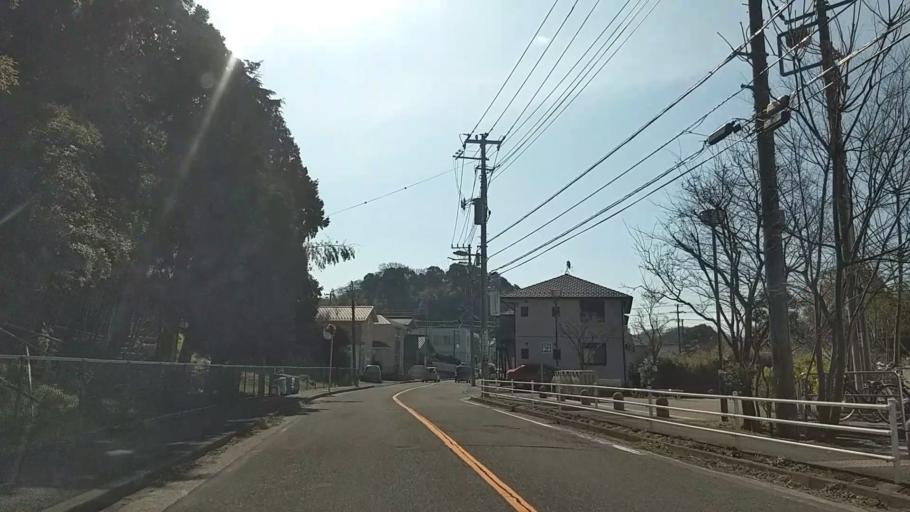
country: JP
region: Kanagawa
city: Kamakura
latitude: 35.4033
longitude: 139.5538
